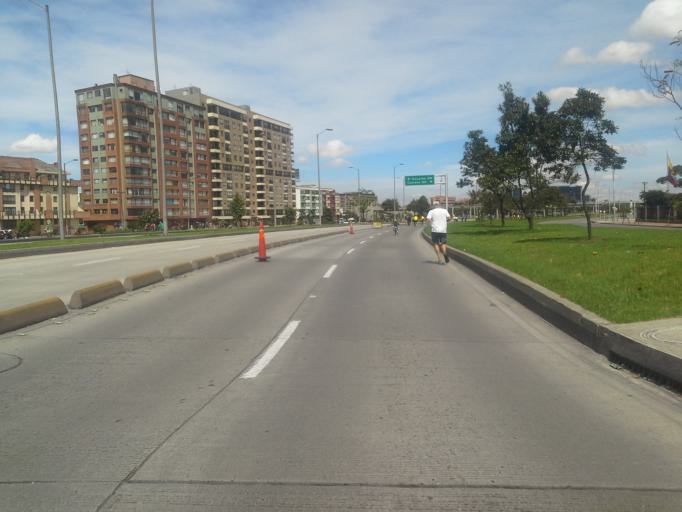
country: CO
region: Bogota D.C.
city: Bogota
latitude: 4.6350
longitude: -74.0908
